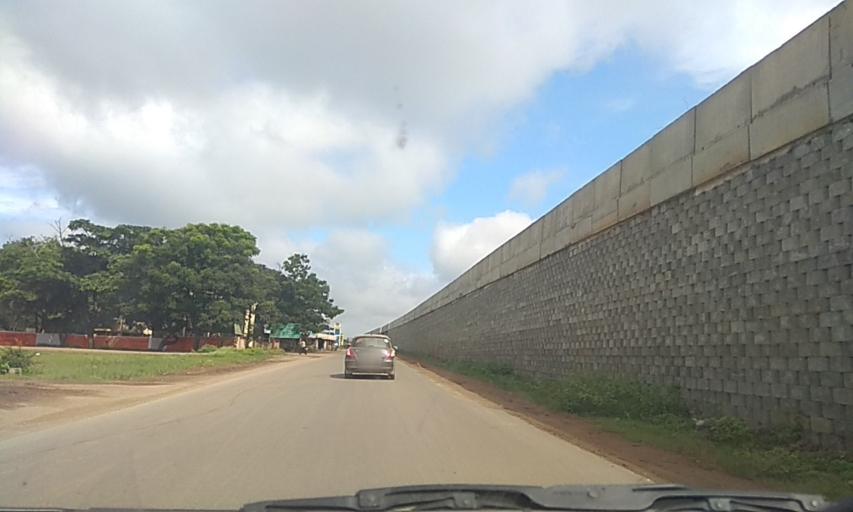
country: IN
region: Karnataka
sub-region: Haveri
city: Shiggaon
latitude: 14.9921
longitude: 75.2161
